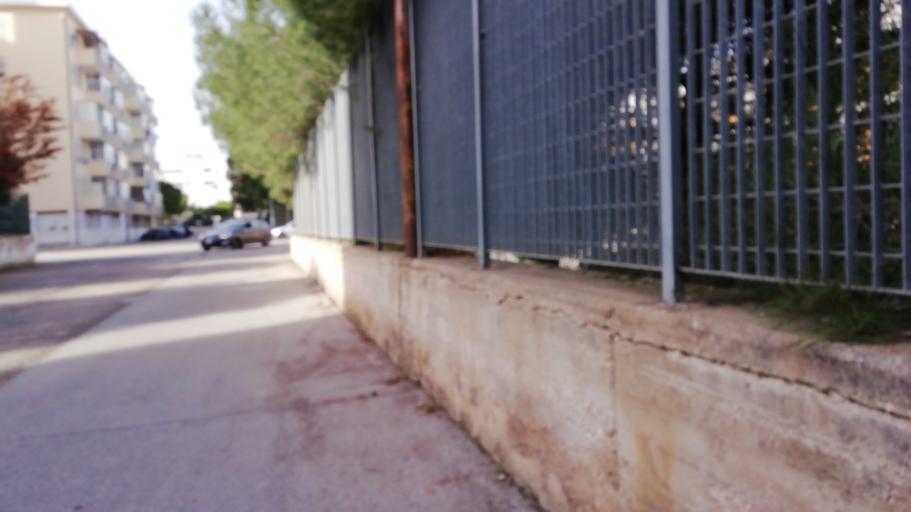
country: IT
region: Apulia
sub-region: Provincia di Bari
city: Triggiano
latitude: 41.1015
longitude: 16.9032
